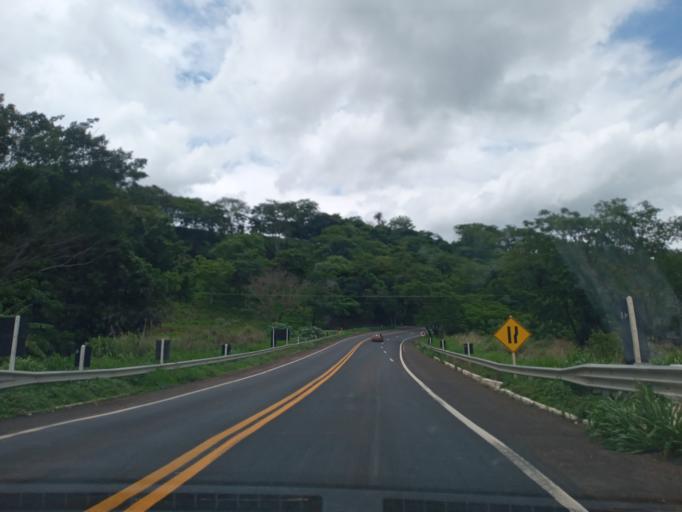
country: BR
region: Minas Gerais
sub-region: Monte Carmelo
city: Monte Carmelo
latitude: -19.2666
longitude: -47.6431
